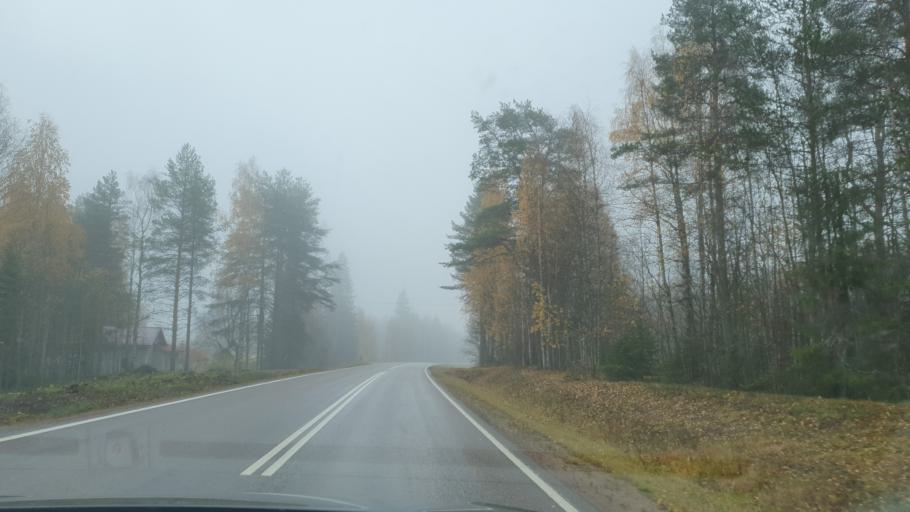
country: FI
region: Lapland
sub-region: Rovaniemi
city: Rovaniemi
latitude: 66.8105
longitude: 25.4069
